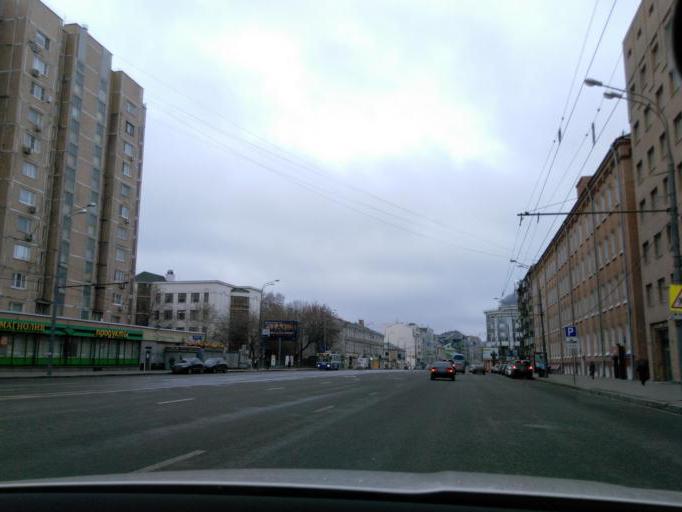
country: RU
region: Moscow
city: Mar'ina Roshcha
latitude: 55.7856
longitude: 37.5950
